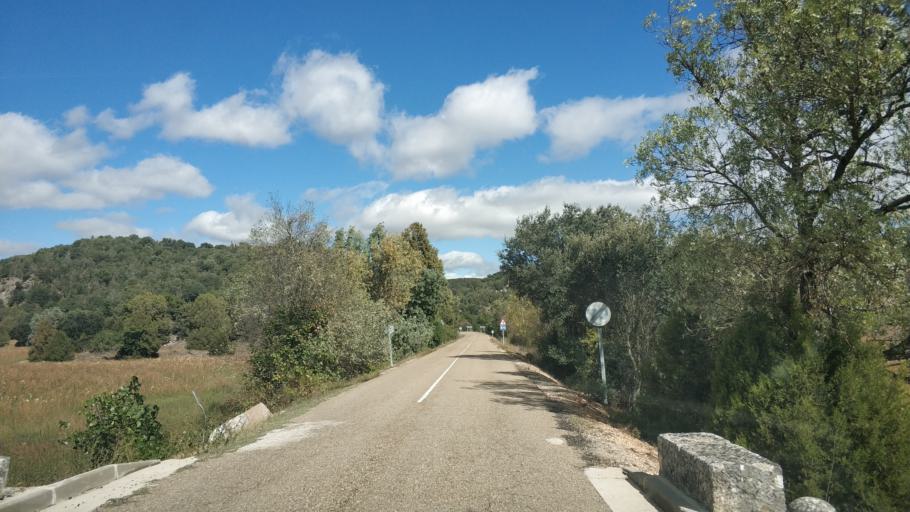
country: ES
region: Castille and Leon
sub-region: Provincia de Burgos
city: Retuerta
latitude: 42.0425
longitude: -3.4717
